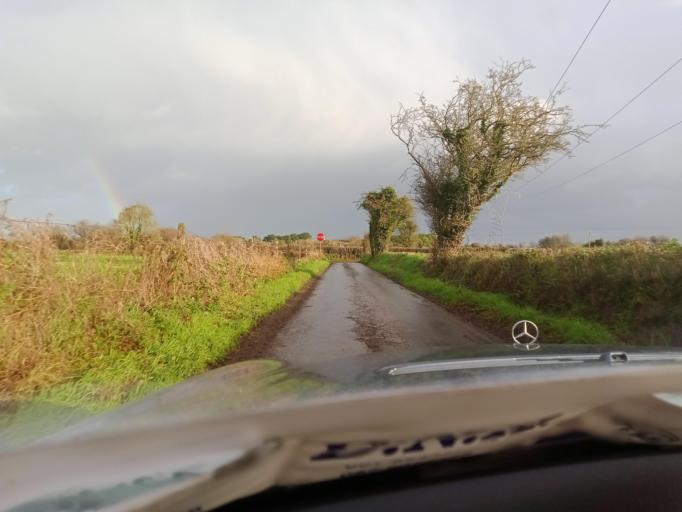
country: IE
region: Leinster
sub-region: Kilkenny
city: Mooncoin
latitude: 52.2791
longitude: -7.1932
